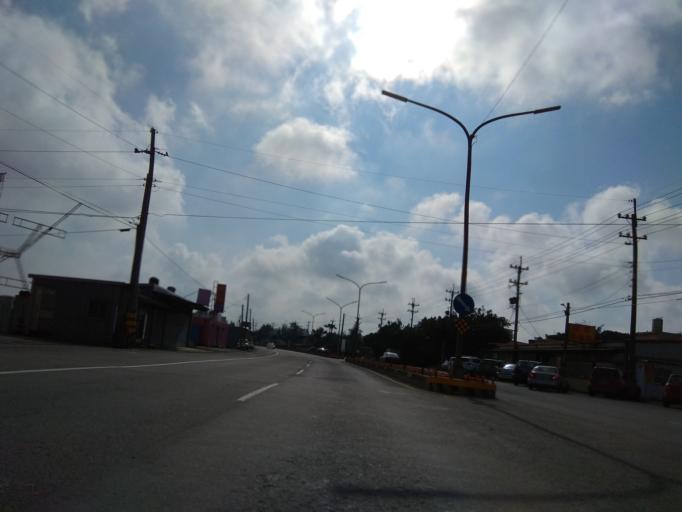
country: TW
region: Taiwan
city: Taoyuan City
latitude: 25.0404
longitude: 121.1038
